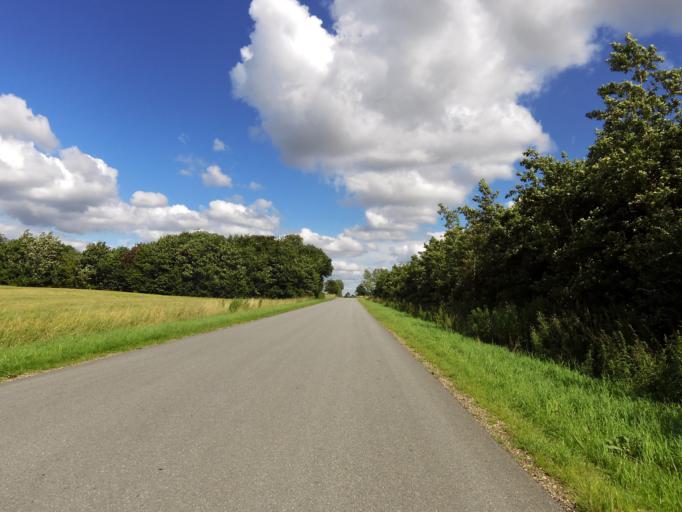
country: DK
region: South Denmark
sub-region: Vejen Kommune
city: Rodding
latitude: 55.3160
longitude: 9.1787
